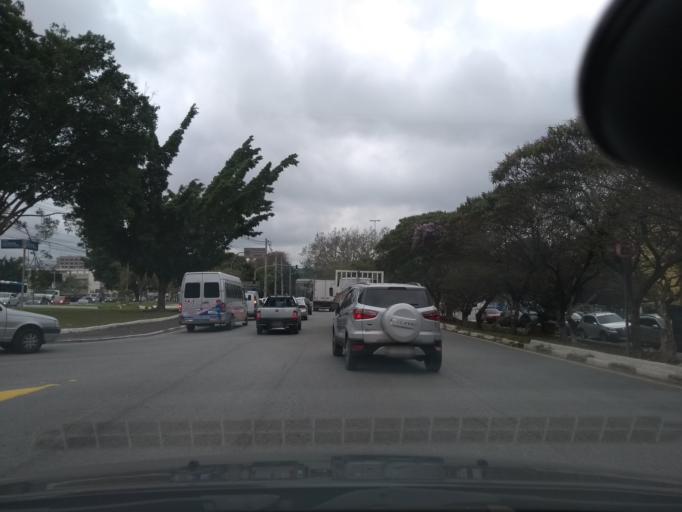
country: BR
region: Sao Paulo
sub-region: Guarulhos
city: Guarulhos
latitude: -23.4593
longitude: -46.4957
